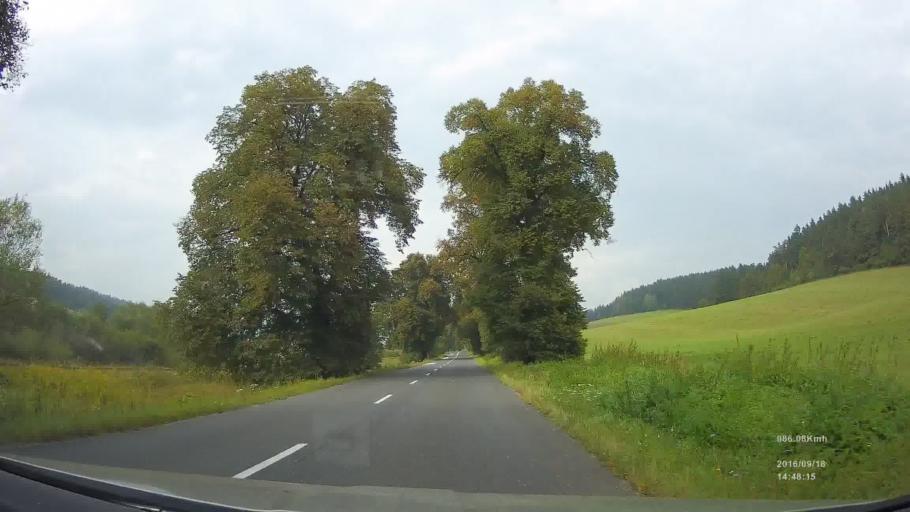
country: SK
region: Kosicky
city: Spisska Nova Ves
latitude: 48.9737
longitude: 20.5821
